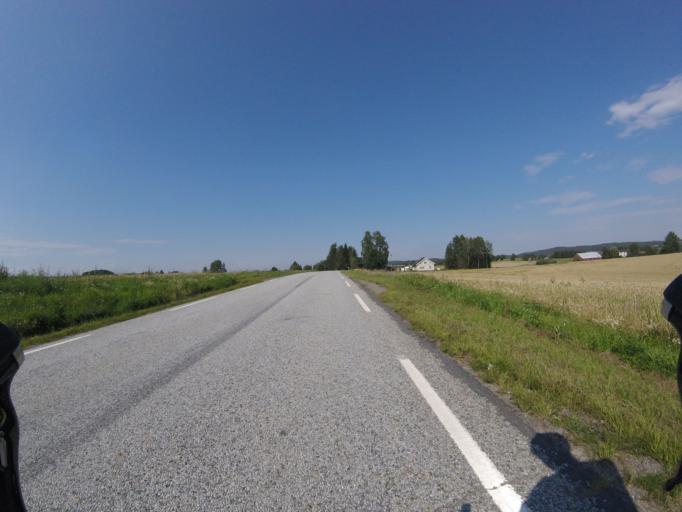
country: NO
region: Akershus
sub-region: Ullensaker
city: Klofta
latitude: 60.0886
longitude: 11.1620
